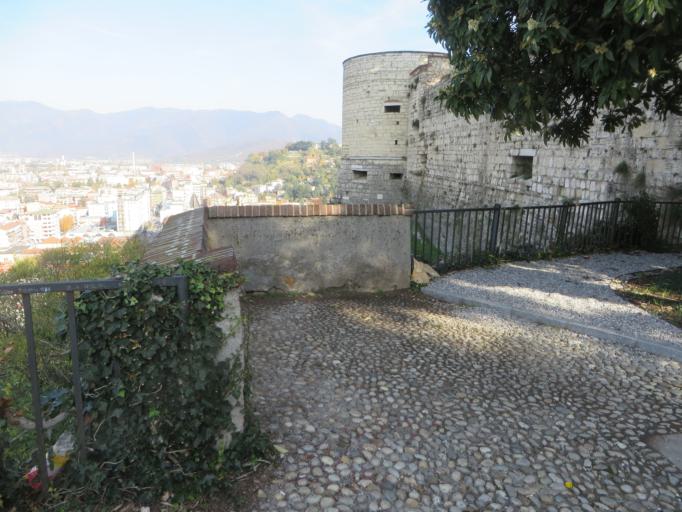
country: IT
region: Lombardy
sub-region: Provincia di Brescia
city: Brescia
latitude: 45.5434
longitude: 10.2242
